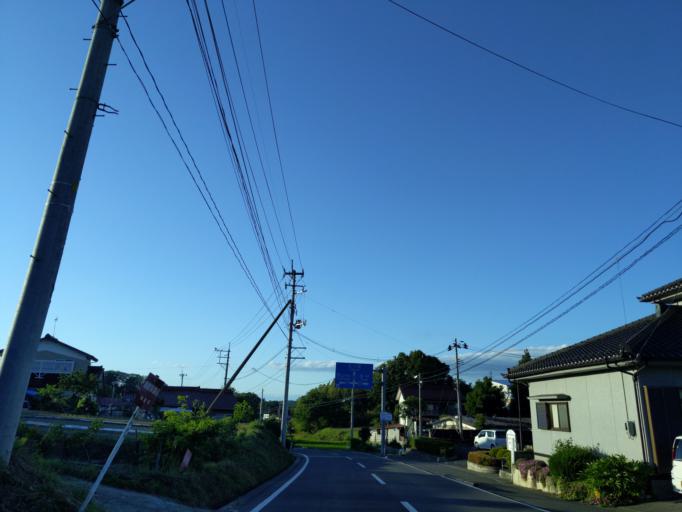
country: JP
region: Fukushima
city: Koriyama
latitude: 37.4046
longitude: 140.4130
